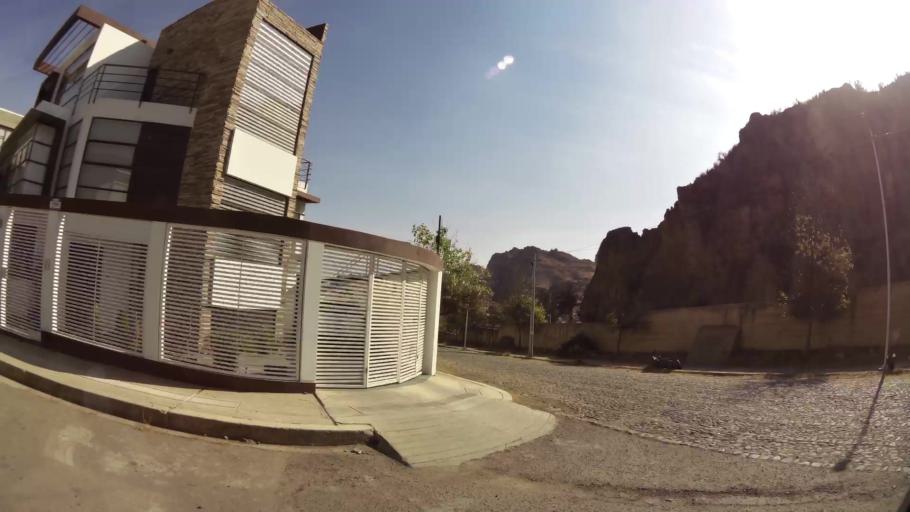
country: BO
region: La Paz
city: La Paz
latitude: -16.5093
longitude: -68.0546
